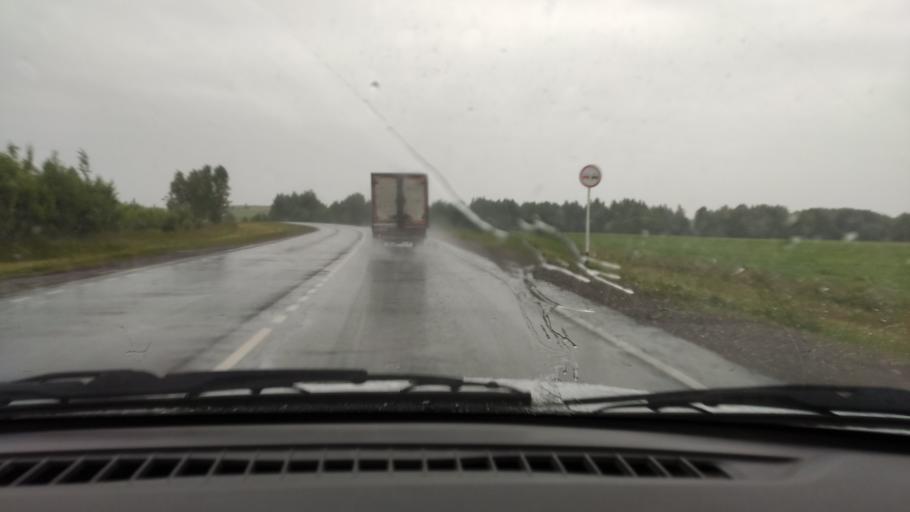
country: RU
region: Perm
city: Chastyye
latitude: 57.3928
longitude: 54.4361
